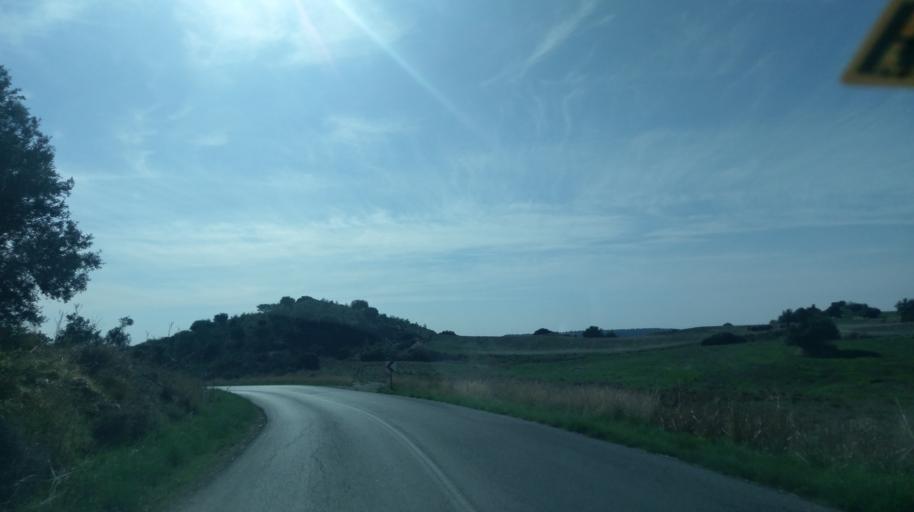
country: CY
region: Ammochostos
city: Trikomo
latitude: 35.3423
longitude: 33.9294
